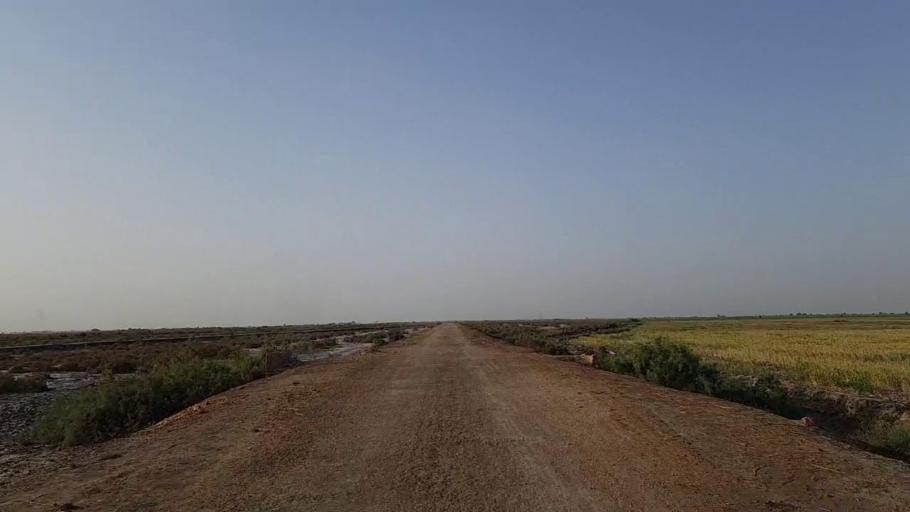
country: PK
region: Sindh
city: Jati
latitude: 24.3525
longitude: 68.1490
